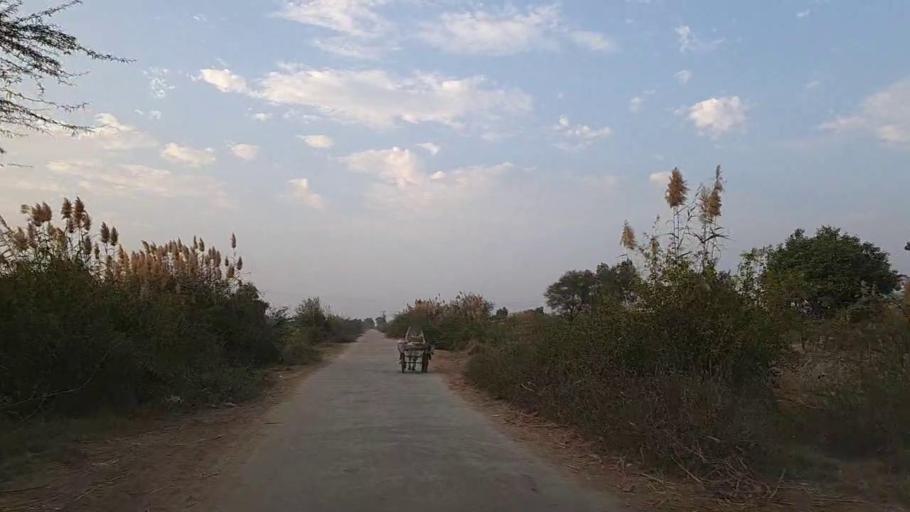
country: PK
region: Sindh
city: Mirwah Gorchani
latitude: 25.3374
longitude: 69.2092
